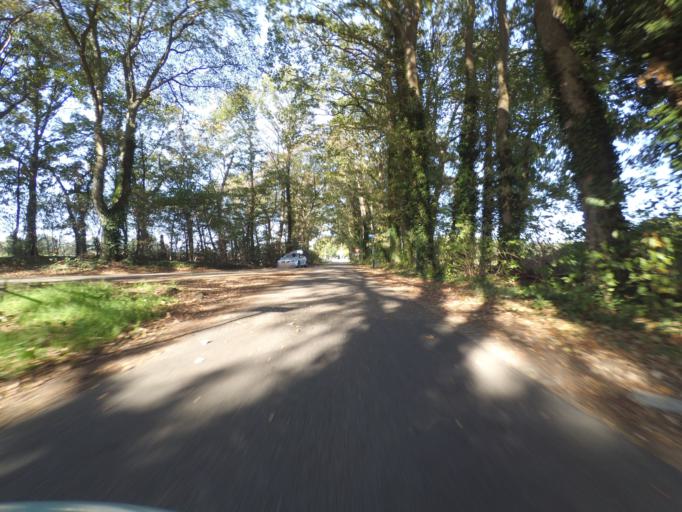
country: NL
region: Gelderland
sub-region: Gemeente Lochem
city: Barchem
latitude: 52.0886
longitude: 6.4658
